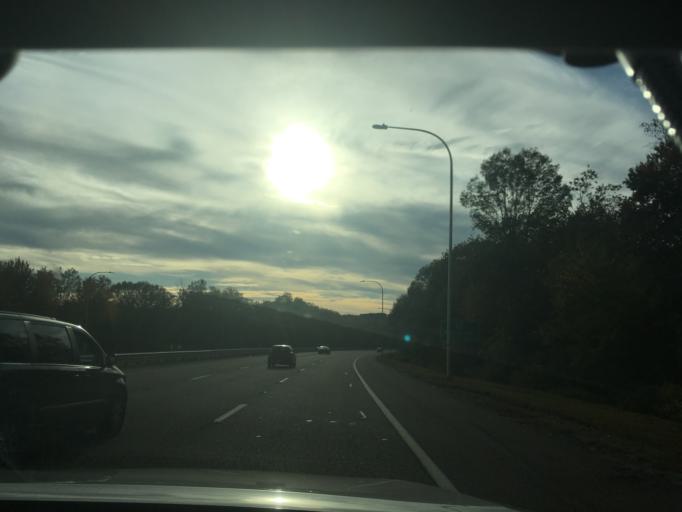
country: US
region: Rhode Island
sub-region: Providence County
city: Johnston
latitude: 41.8181
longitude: -71.4843
